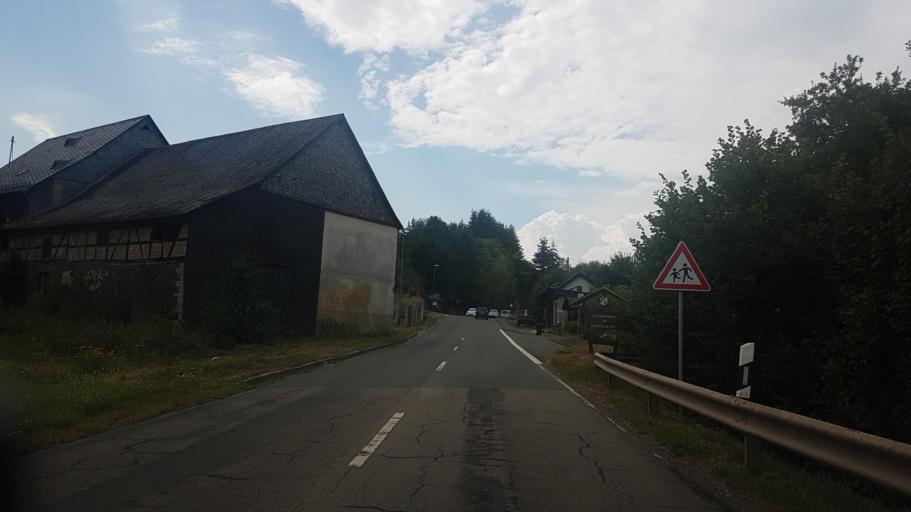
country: DE
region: Rheinland-Pfalz
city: Dienstweiler
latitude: 49.6364
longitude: 7.1869
